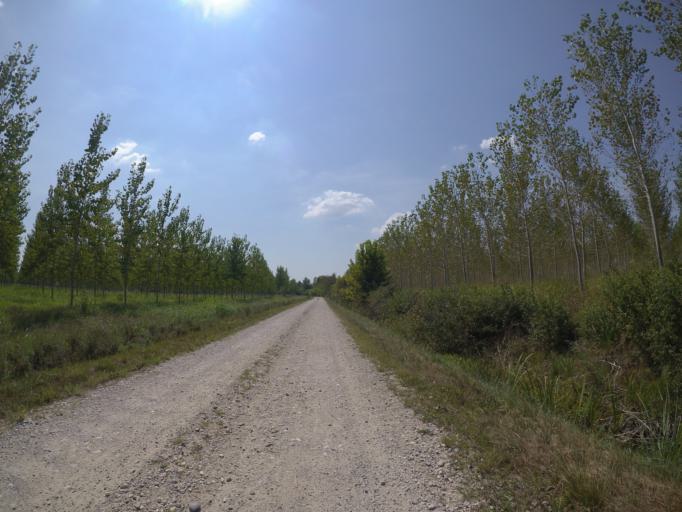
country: IT
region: Friuli Venezia Giulia
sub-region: Provincia di Udine
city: Bertiolo
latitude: 45.9216
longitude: 13.0639
